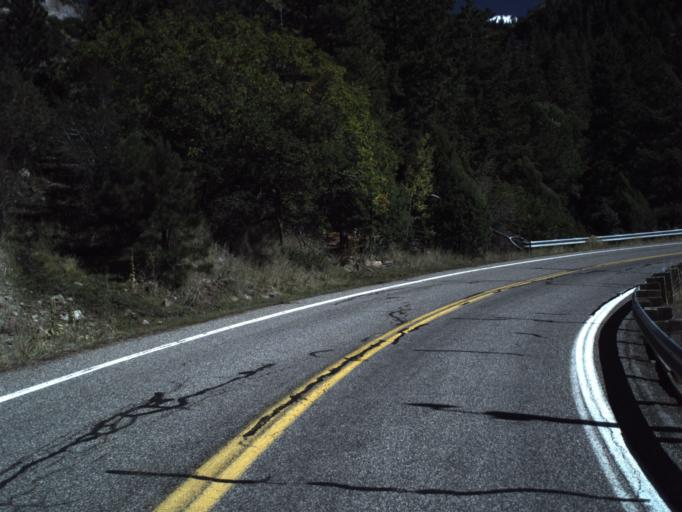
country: US
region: Utah
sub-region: Beaver County
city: Beaver
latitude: 38.2699
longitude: -112.4804
